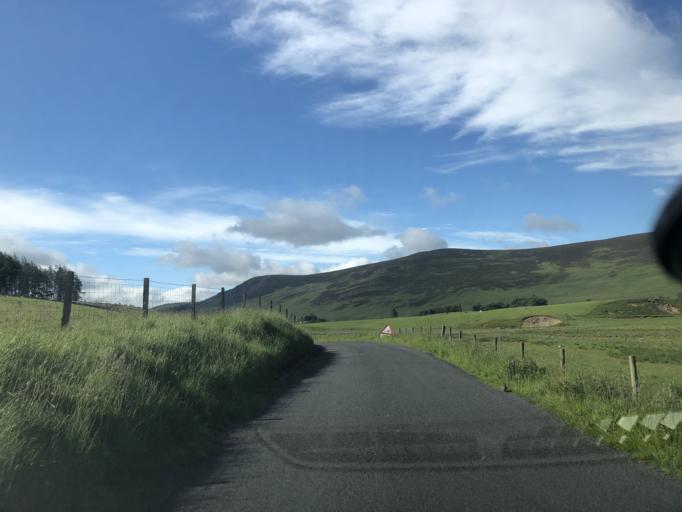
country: GB
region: Scotland
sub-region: Angus
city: Kirriemuir
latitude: 56.8035
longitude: -3.0372
